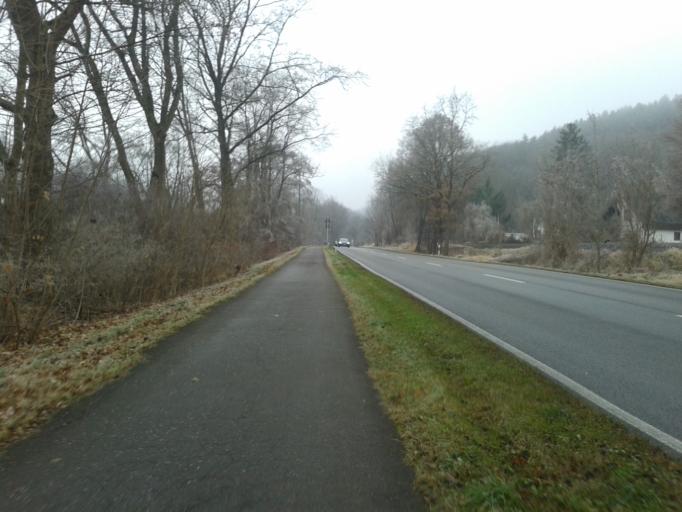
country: DE
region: Bavaria
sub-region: Swabia
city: Neu-Ulm
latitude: 48.4312
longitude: 10.0445
